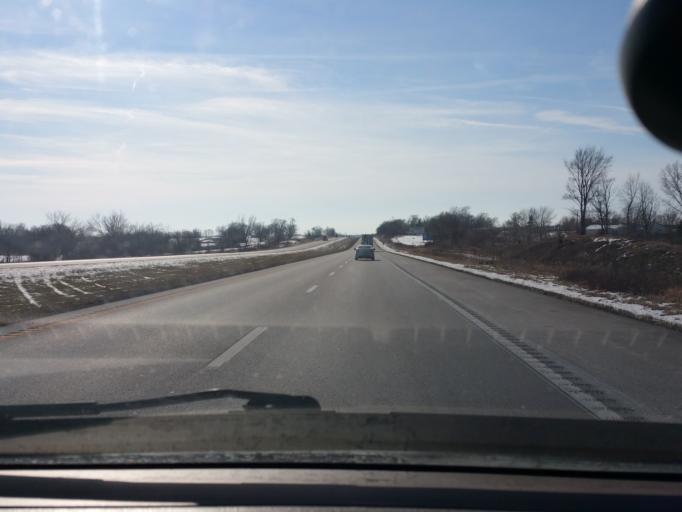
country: US
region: Missouri
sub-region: Clinton County
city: Cameron
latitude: 39.7945
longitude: -94.2032
